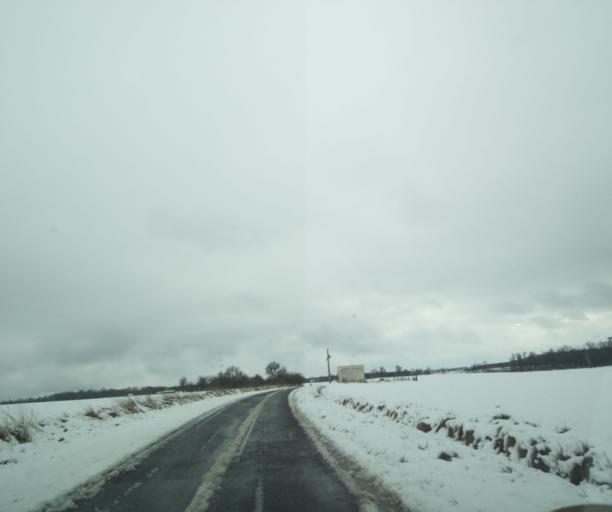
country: FR
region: Champagne-Ardenne
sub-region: Departement de la Haute-Marne
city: Montier-en-Der
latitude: 48.4184
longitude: 4.7326
